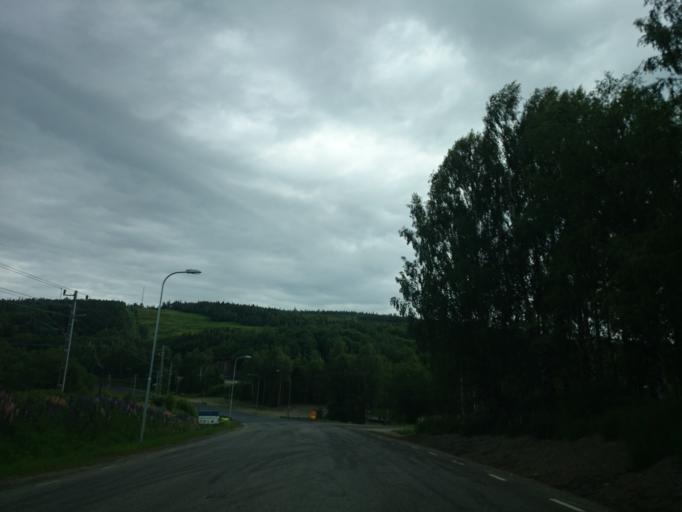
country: SE
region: Vaesternorrland
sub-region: Timra Kommun
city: Timra
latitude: 62.4732
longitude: 17.3144
